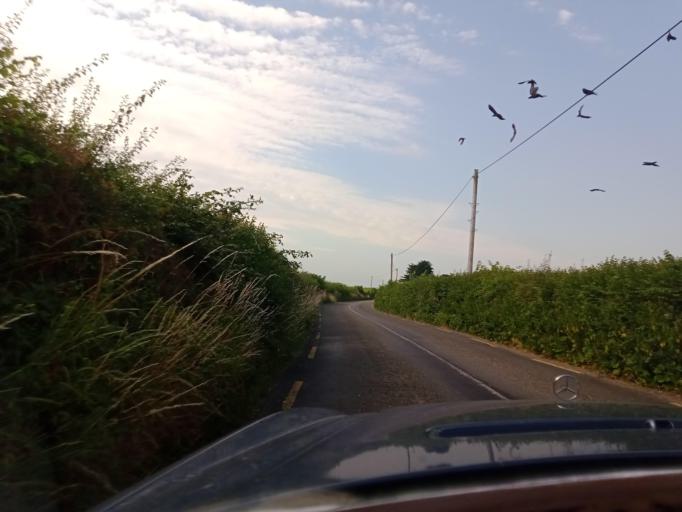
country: IE
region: Leinster
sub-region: Kilkenny
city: Callan
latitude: 52.5095
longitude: -7.3120
